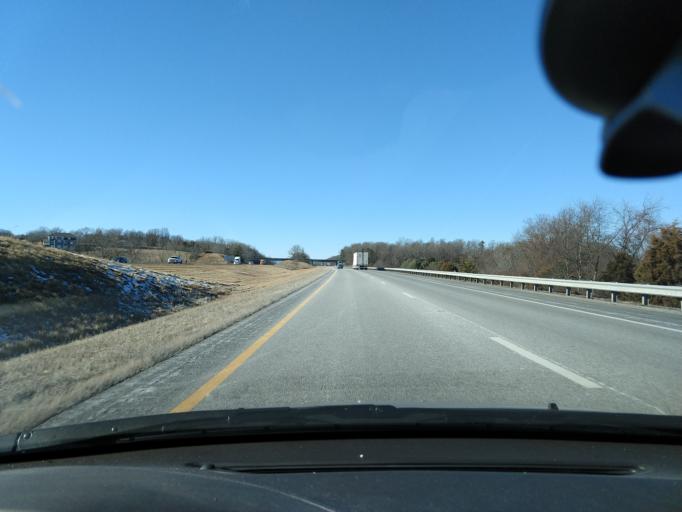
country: US
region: Virginia
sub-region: Augusta County
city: Fishersville
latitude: 38.1024
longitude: -79.0087
